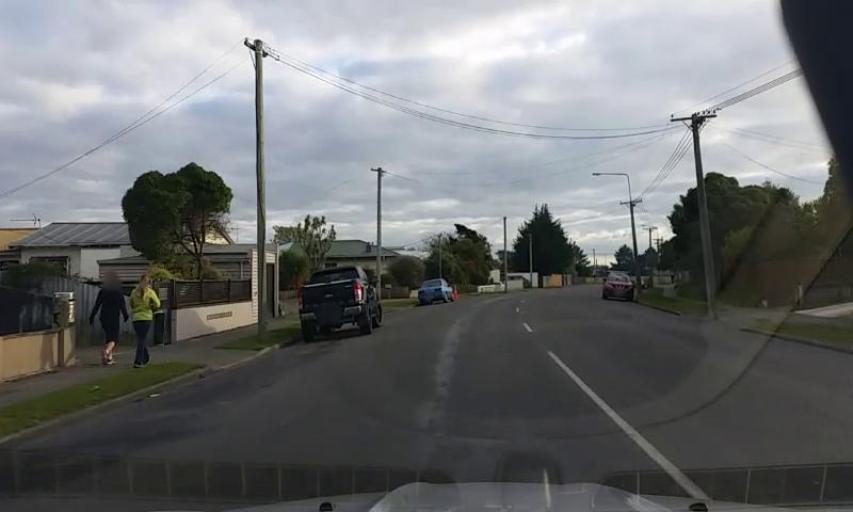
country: NZ
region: Canterbury
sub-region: Christchurch City
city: Christchurch
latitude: -43.5163
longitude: 172.7294
